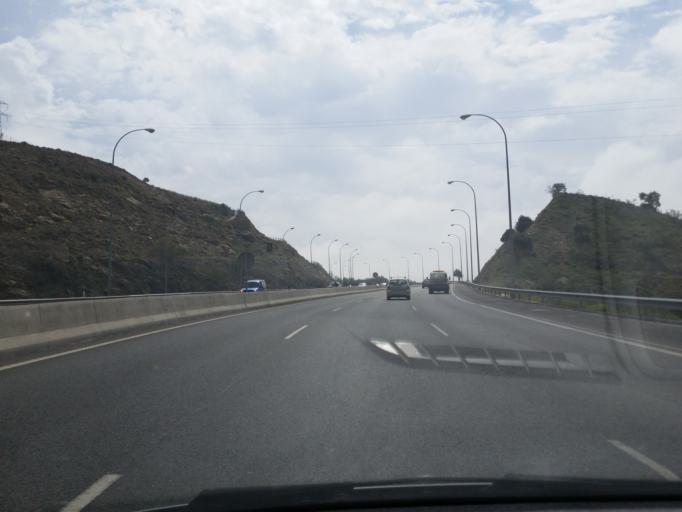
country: ES
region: Andalusia
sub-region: Provincia de Malaga
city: Malaga
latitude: 36.7548
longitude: -4.4164
